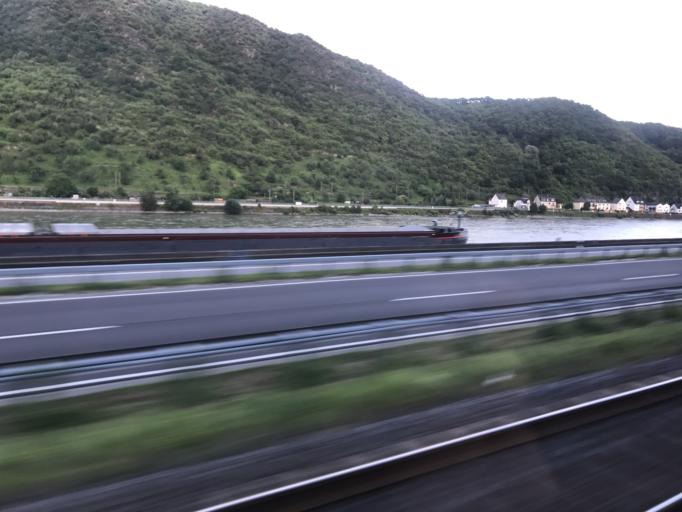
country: DE
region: Rheinland-Pfalz
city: Kestert
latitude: 50.1938
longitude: 7.6439
